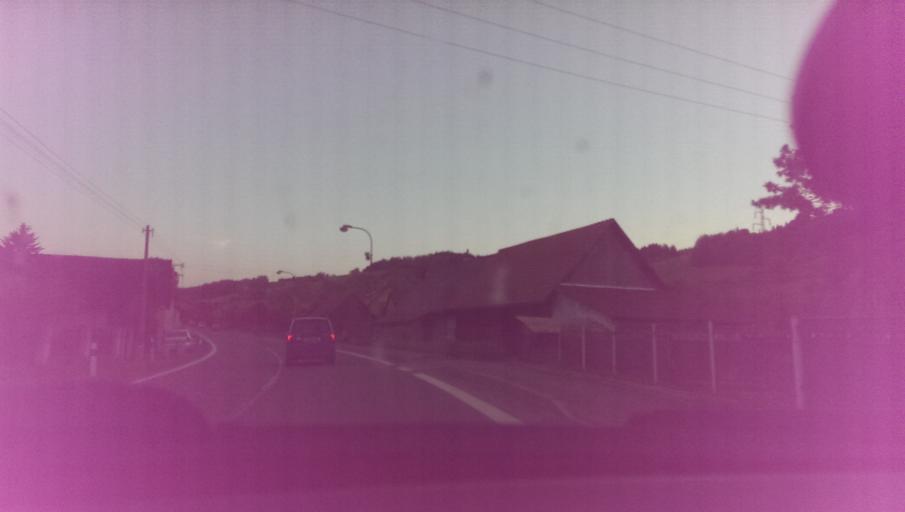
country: CZ
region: Zlin
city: Valasska Polanka
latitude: 49.2905
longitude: 17.9993
